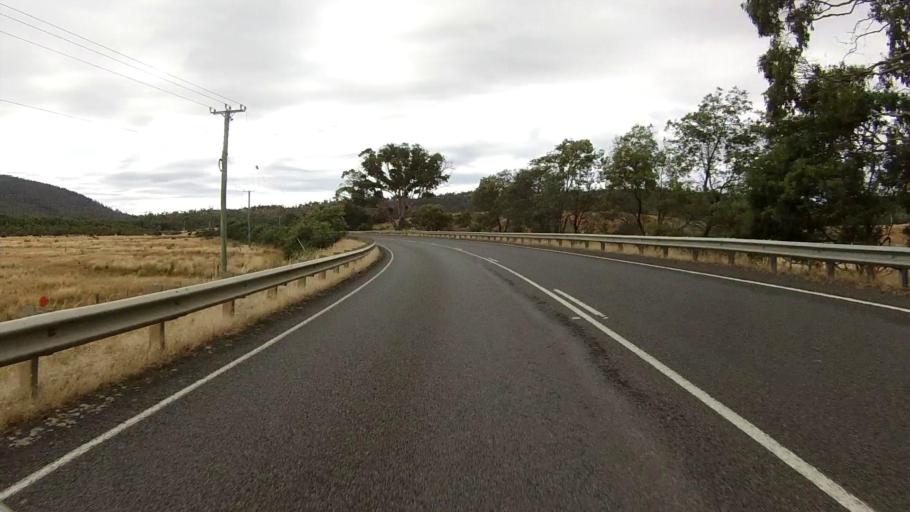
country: AU
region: Tasmania
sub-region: Sorell
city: Sorell
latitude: -42.5958
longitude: 147.7860
